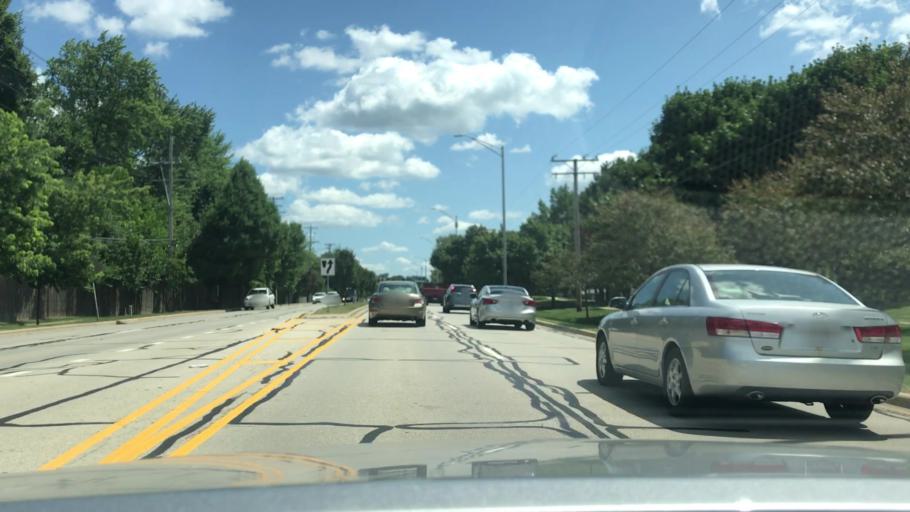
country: US
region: Illinois
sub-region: DuPage County
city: Naperville
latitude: 41.7662
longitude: -88.1772
